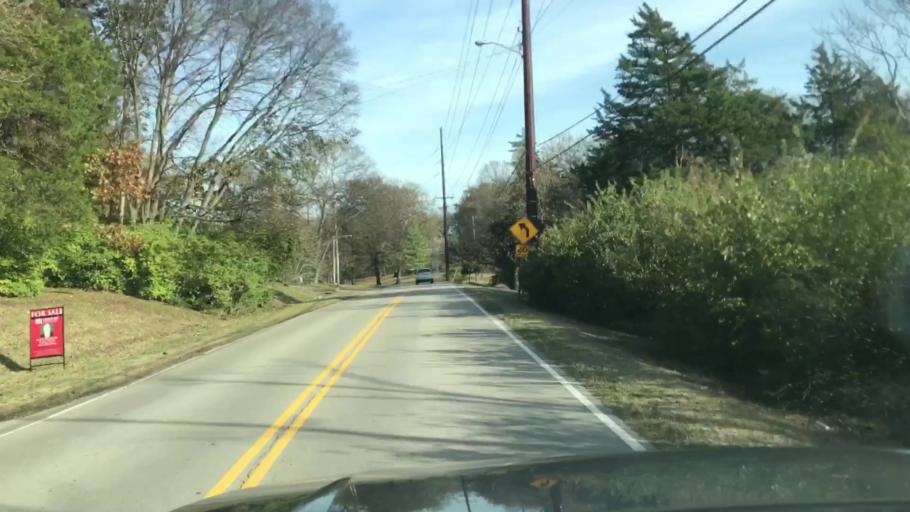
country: US
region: Tennessee
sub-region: Davidson County
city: Belle Meade
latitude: 36.1174
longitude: -86.8953
